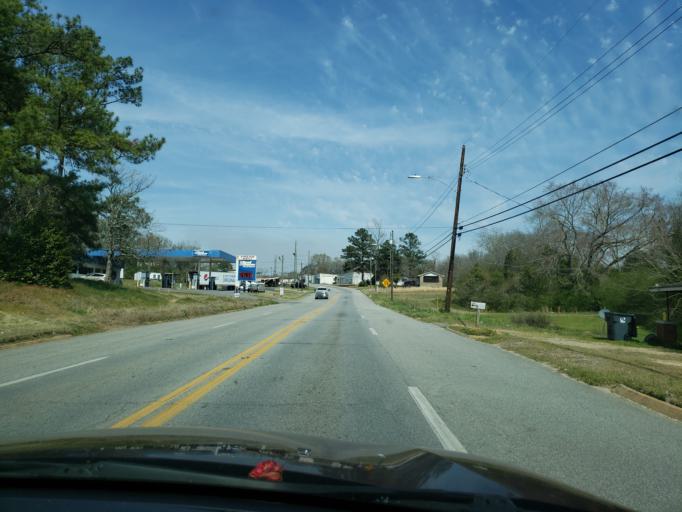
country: US
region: Alabama
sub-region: Elmore County
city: Tallassee
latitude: 32.5418
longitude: -85.8749
